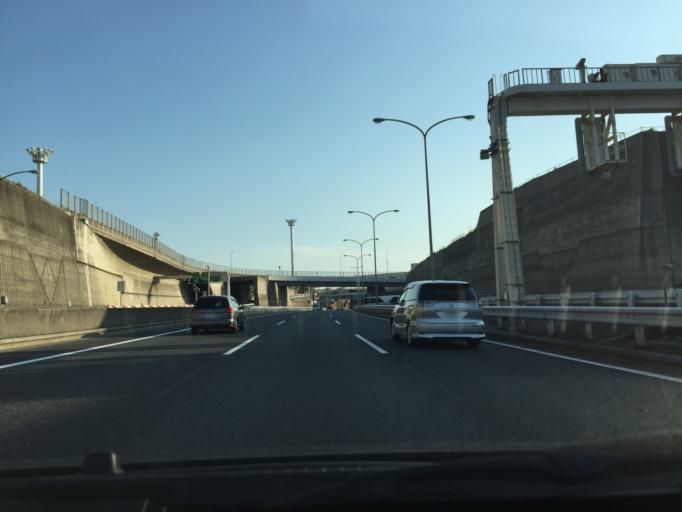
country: JP
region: Kanagawa
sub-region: Kawasaki-shi
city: Kawasaki
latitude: 35.5160
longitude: 139.7902
